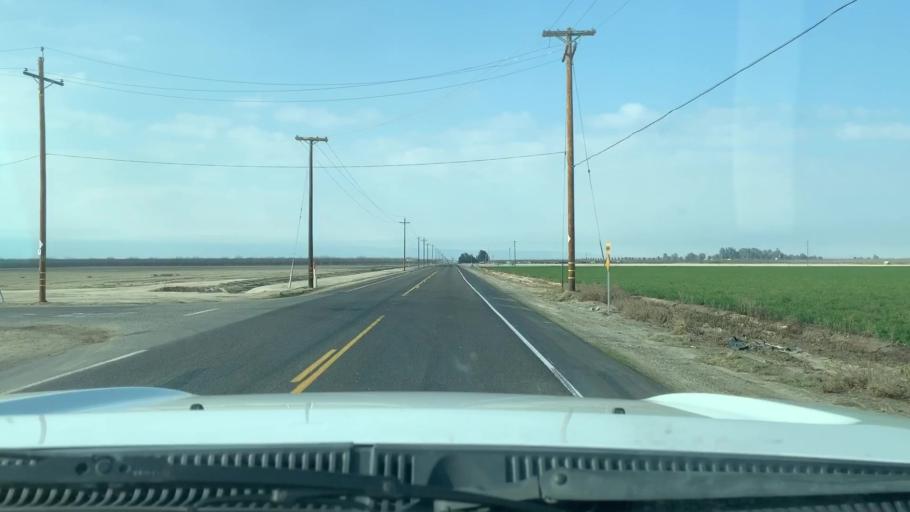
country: US
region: California
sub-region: Kern County
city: Buttonwillow
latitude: 35.4422
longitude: -119.4113
